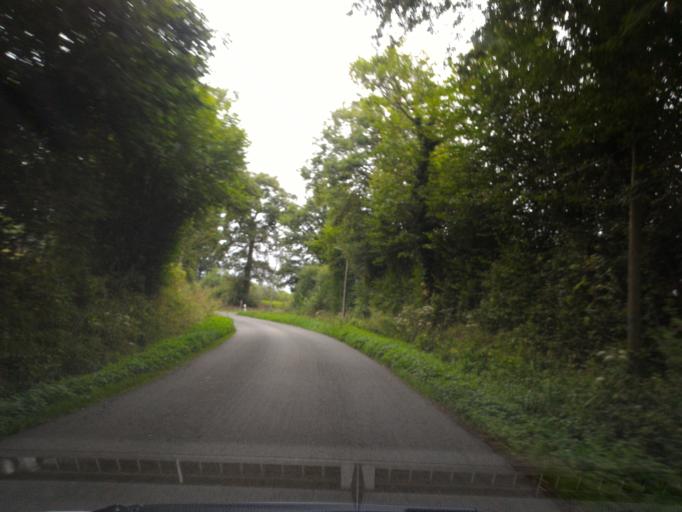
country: FR
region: Poitou-Charentes
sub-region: Departement de la Charente
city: Etagnac
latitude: 45.9437
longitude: 0.7970
